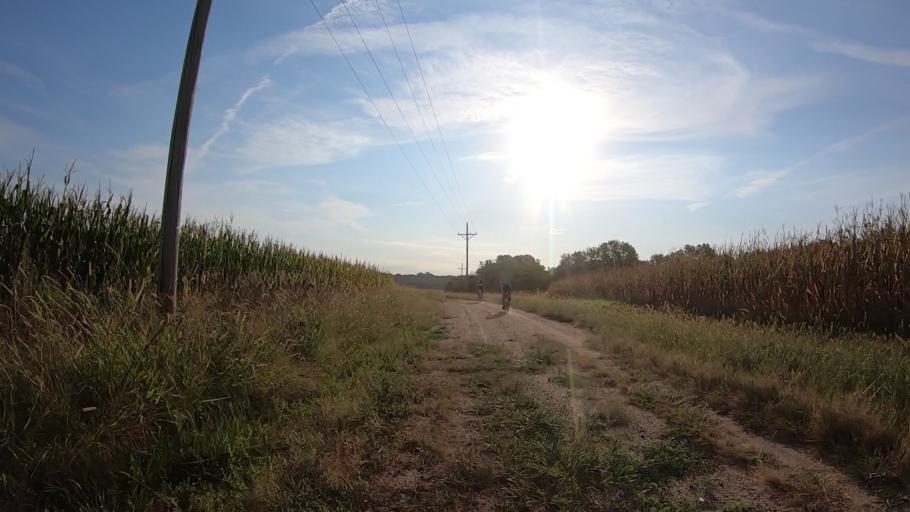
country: US
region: Kansas
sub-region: Marshall County
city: Blue Rapids
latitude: 39.7118
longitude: -96.7835
